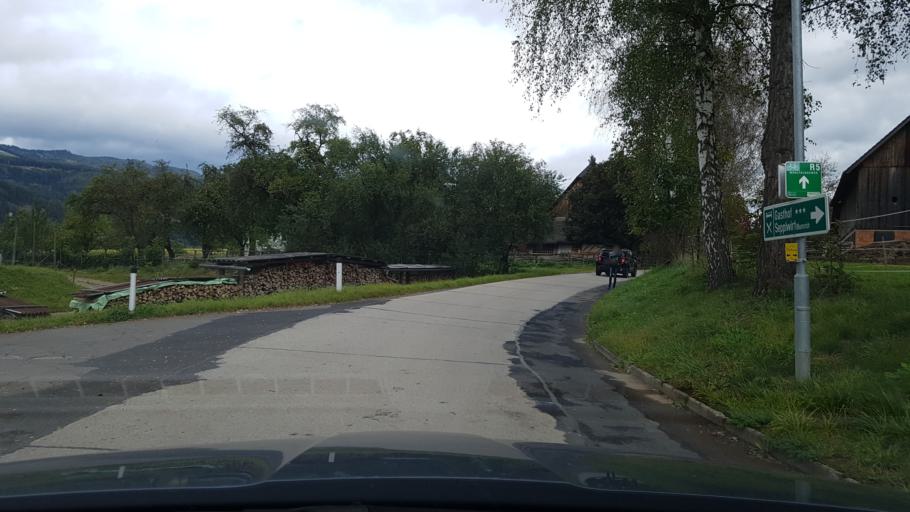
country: AT
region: Styria
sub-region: Politischer Bezirk Bruck-Muerzzuschlag
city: Allerheiligen im Muerztal
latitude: 47.4748
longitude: 15.4000
